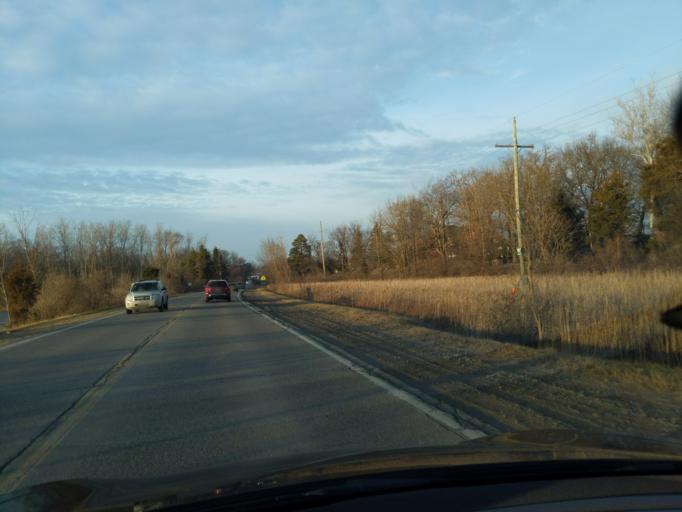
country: US
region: Michigan
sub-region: Livingston County
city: Brighton
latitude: 42.5576
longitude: -83.7547
